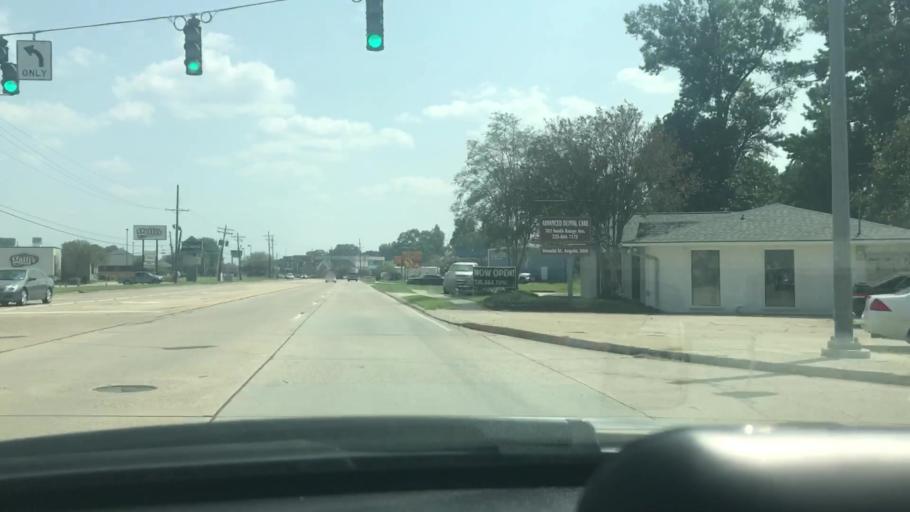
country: US
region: Louisiana
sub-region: Livingston Parish
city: Denham Springs
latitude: 30.4764
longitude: -90.9563
